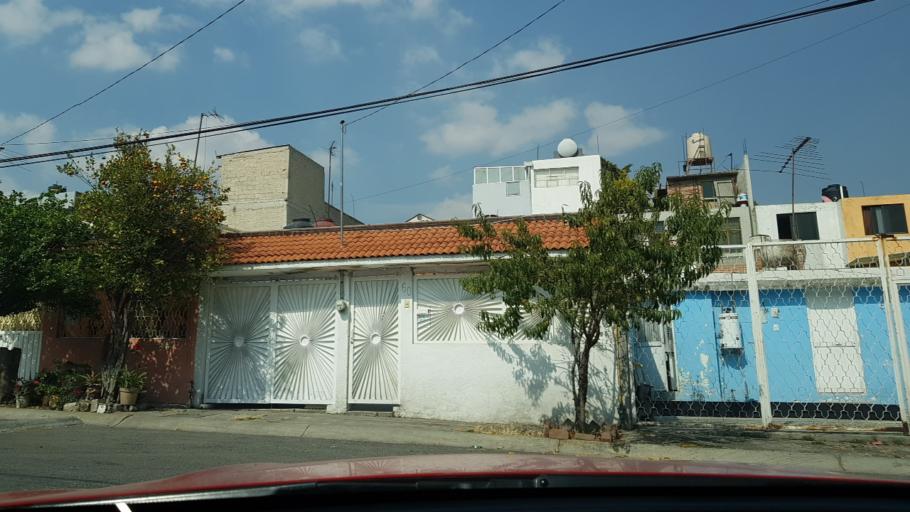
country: MX
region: Mexico
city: Cuautitlan Izcalli
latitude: 19.6469
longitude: -99.2120
